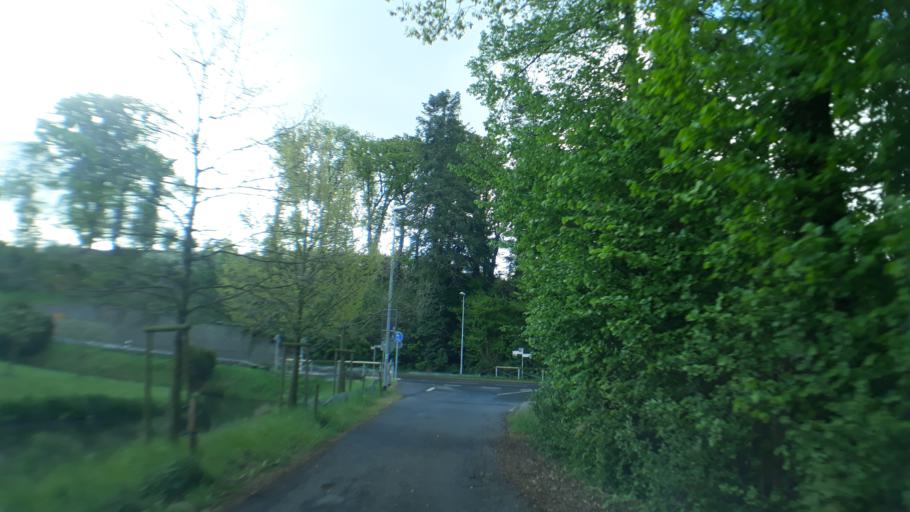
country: DE
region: North Rhine-Westphalia
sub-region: Regierungsbezirk Koln
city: Mechernich
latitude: 50.6235
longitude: 6.6202
